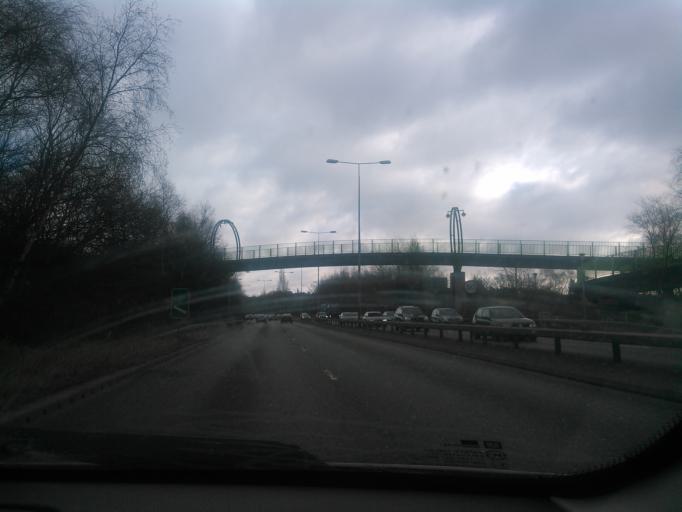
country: GB
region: England
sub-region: Staffordshire
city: Longton
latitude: 52.9831
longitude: -2.1284
